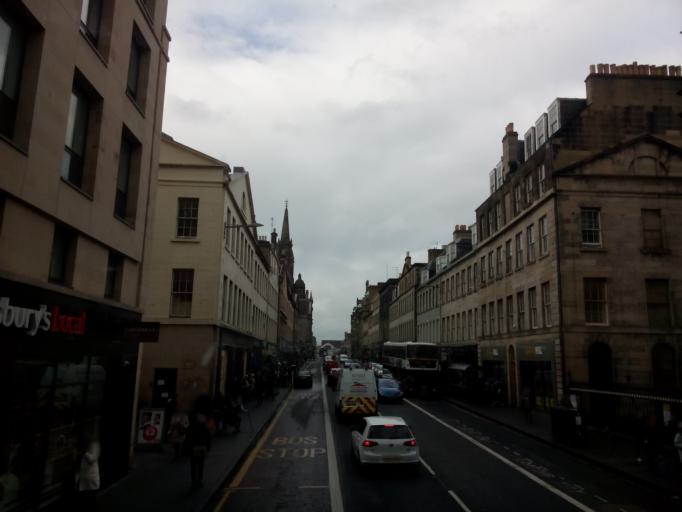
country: GB
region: Scotland
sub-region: Edinburgh
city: Edinburgh
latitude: 55.9484
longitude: -3.1867
